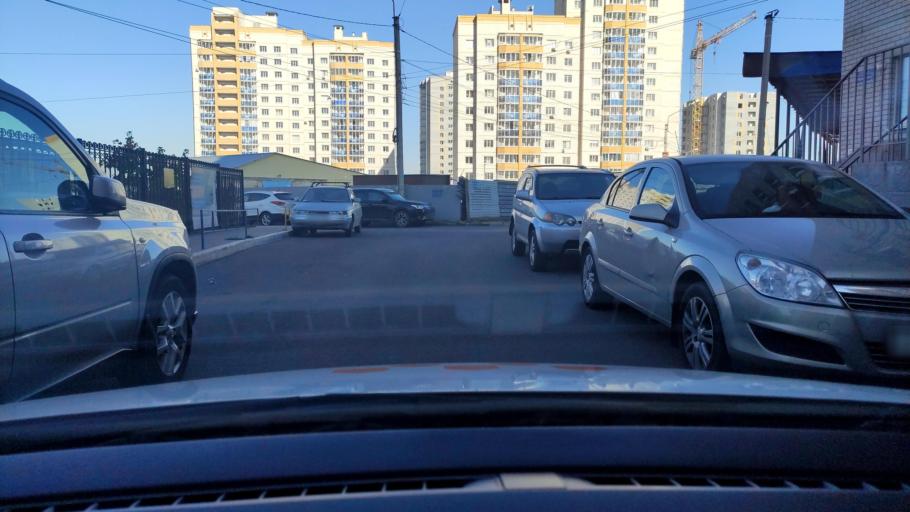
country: RU
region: Voronezj
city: Podgornoye
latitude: 51.7204
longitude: 39.1414
